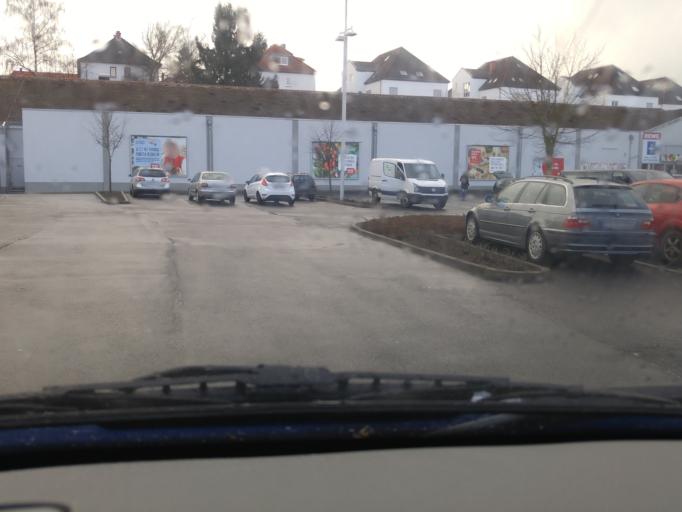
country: DE
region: Hesse
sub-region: Regierungsbezirk Darmstadt
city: Friedberg
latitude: 50.3280
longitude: 8.7514
